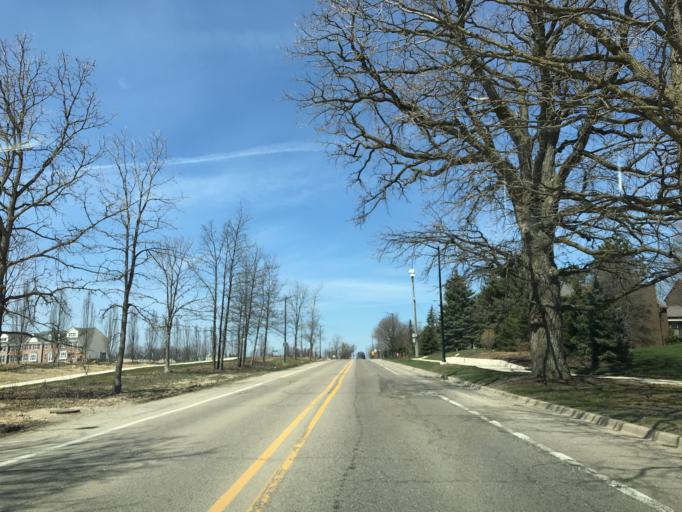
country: US
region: Michigan
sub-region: Washtenaw County
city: Ann Arbor
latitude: 42.3137
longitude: -83.7075
